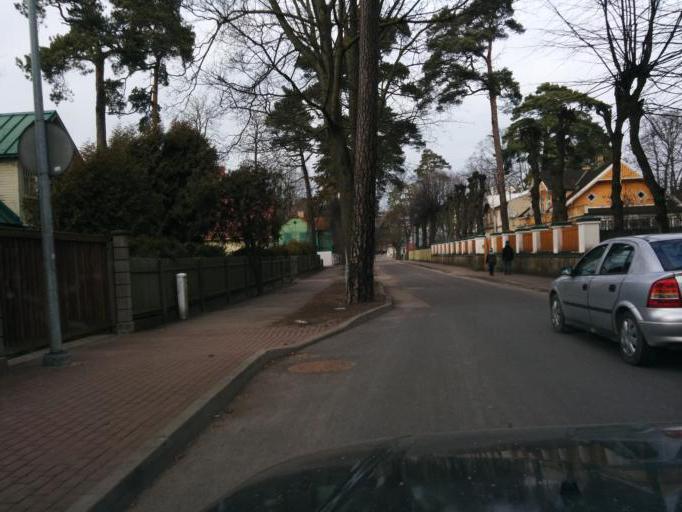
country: LV
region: Jurmala
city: Jurmala
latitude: 56.9729
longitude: 23.7965
